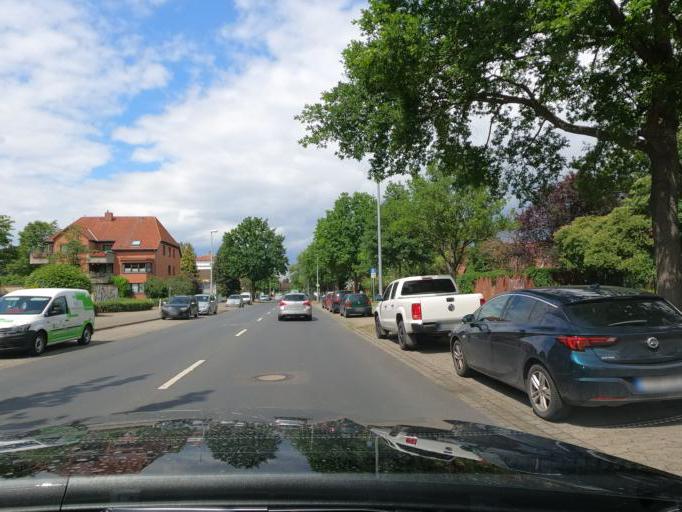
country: DE
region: Lower Saxony
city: Isernhagen Farster Bauerschaft
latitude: 52.3974
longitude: 9.8149
